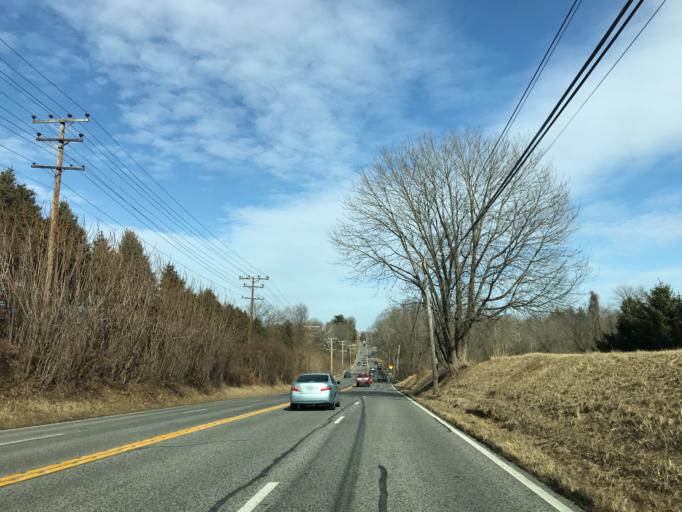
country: US
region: Maryland
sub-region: Baltimore County
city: Kingsville
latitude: 39.4388
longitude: -76.4277
